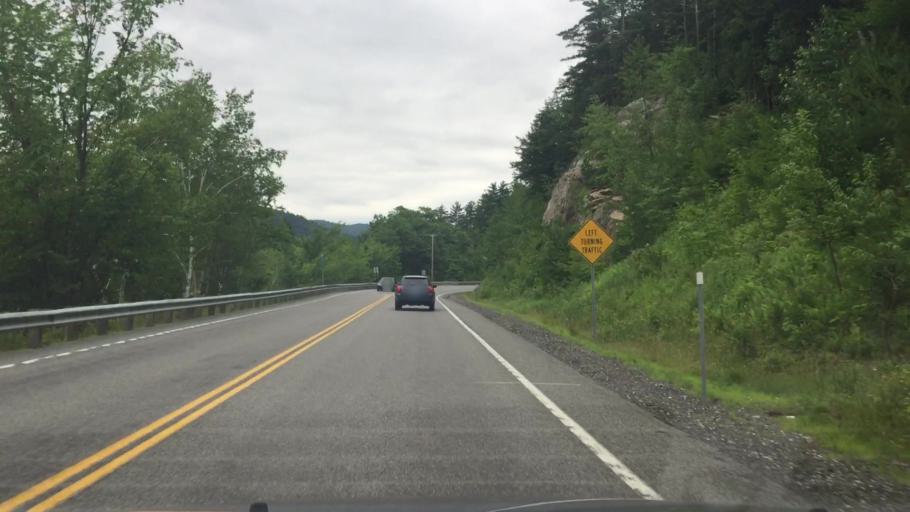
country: US
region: New Hampshire
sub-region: Carroll County
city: North Conway
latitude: 44.0775
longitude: -71.3207
